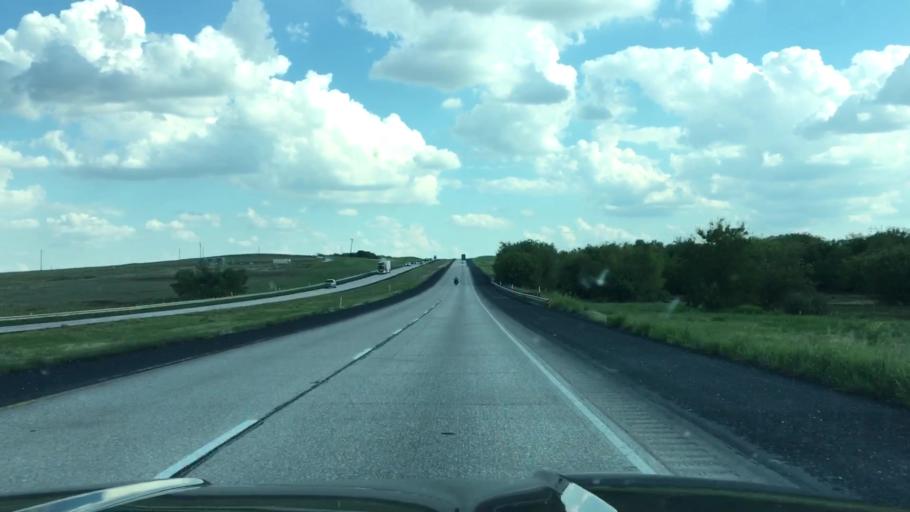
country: US
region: Texas
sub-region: Wise County
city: New Fairview
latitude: 33.1363
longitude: -97.4958
